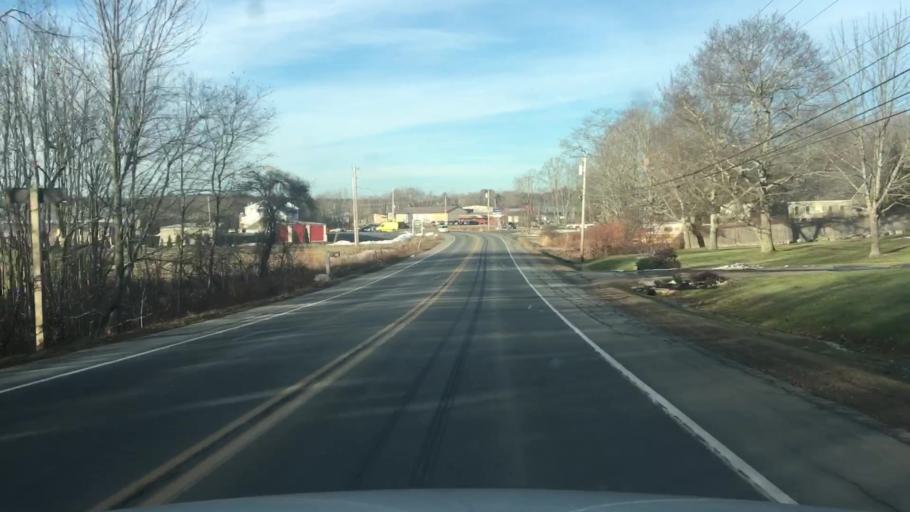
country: US
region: Maine
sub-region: Lincoln County
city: Wiscasset
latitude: 44.0353
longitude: -69.6727
